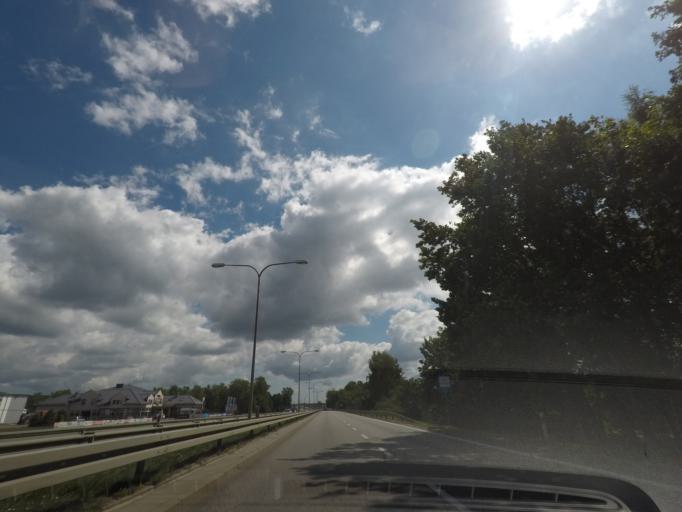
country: PL
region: Pomeranian Voivodeship
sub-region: Powiat wejherowski
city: Wejherowo
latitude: 54.6087
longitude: 18.2063
